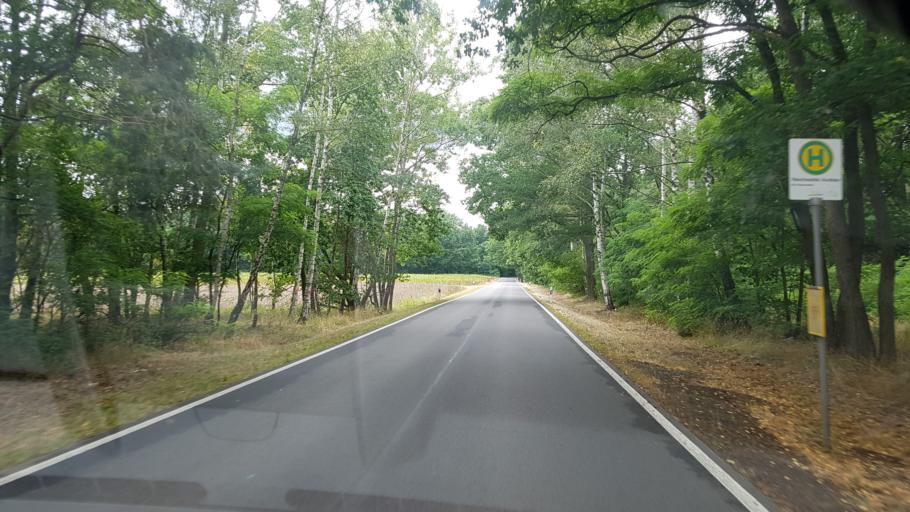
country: DE
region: Saxony
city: Mucka
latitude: 51.3804
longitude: 14.6797
